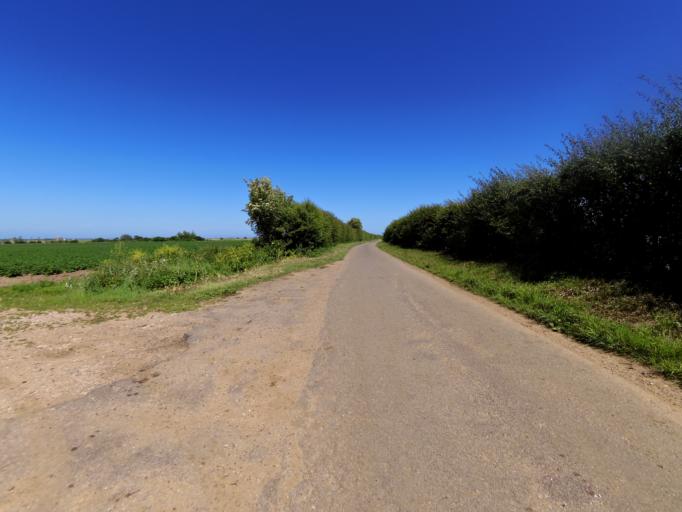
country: GB
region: England
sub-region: Suffolk
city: Felixstowe
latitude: 52.0086
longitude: 1.4275
